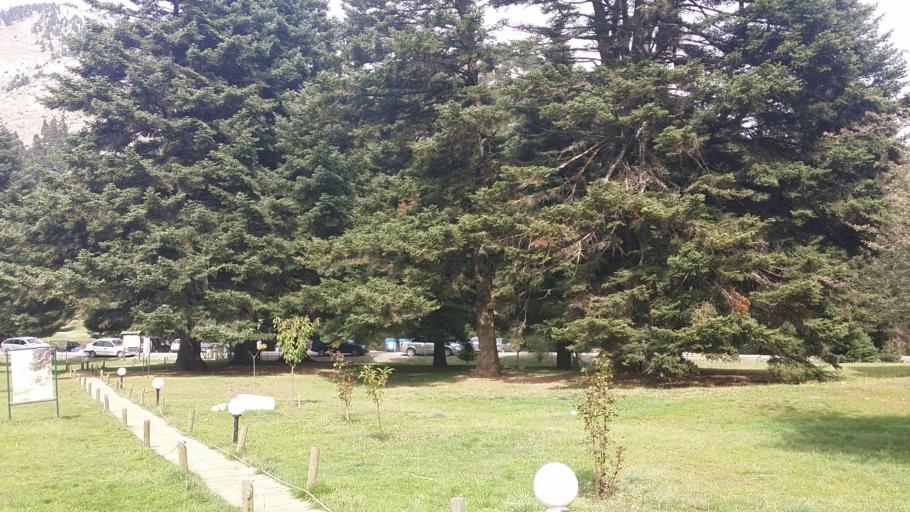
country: GR
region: Central Greece
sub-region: Nomos Voiotias
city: Ayia Trias
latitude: 38.3217
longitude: 22.8546
